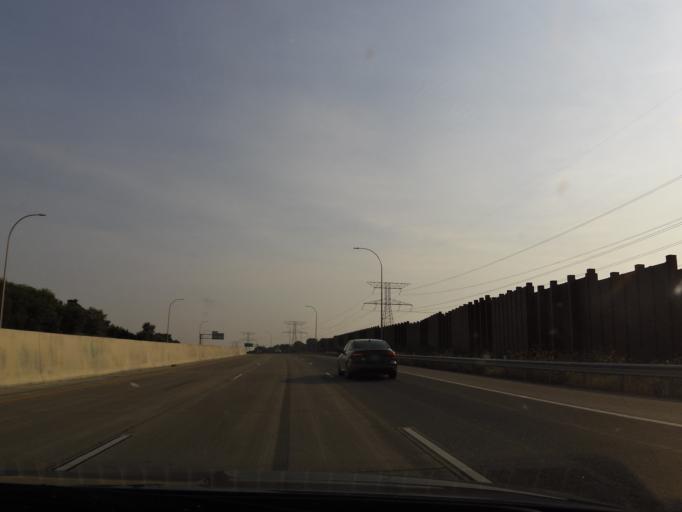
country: US
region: Minnesota
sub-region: Hennepin County
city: Maple Grove
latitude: 45.0584
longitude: -93.4511
